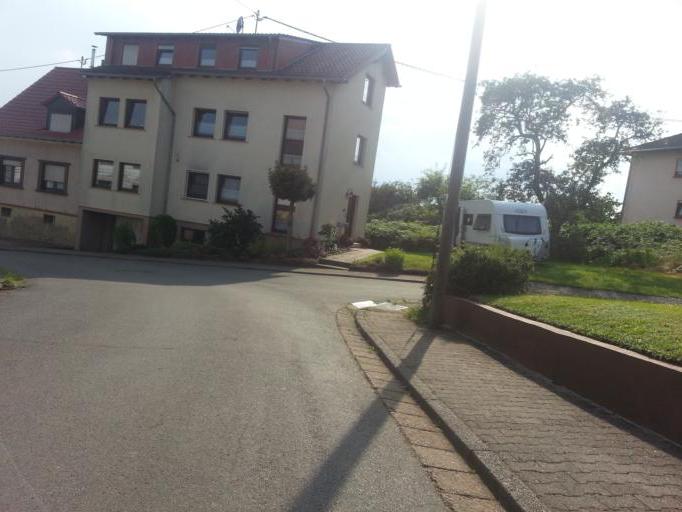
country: DE
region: Saarland
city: Oberthal
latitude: 49.5104
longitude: 7.0973
